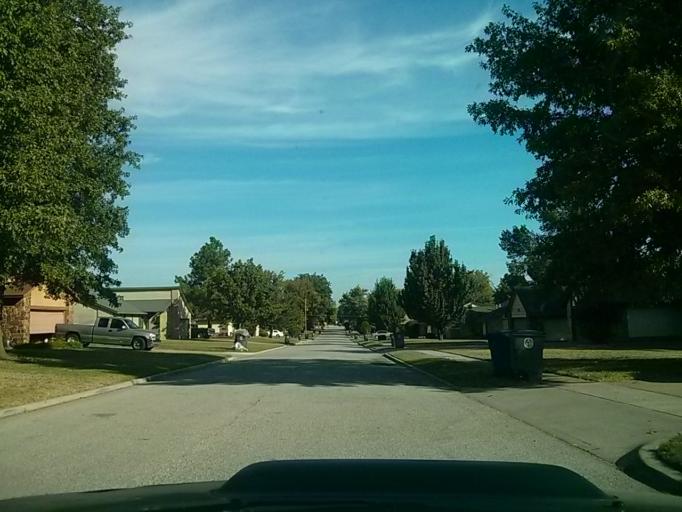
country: US
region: Oklahoma
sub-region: Tulsa County
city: Tulsa
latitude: 36.1698
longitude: -95.9923
